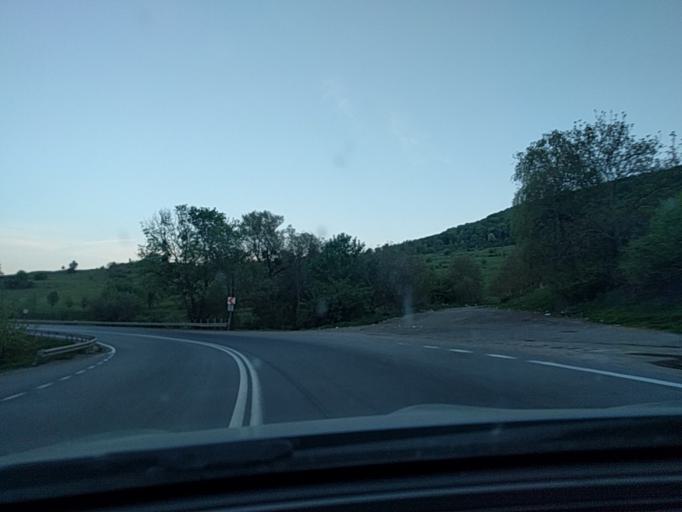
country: RO
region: Mures
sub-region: Comuna Nades
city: Nades
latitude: 46.2899
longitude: 24.7162
